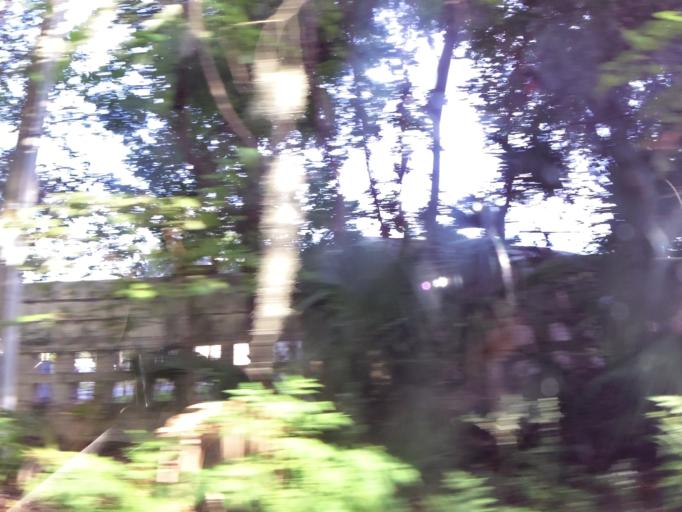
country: US
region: Florida
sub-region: Duval County
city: Jacksonville
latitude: 30.3687
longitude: -81.6542
